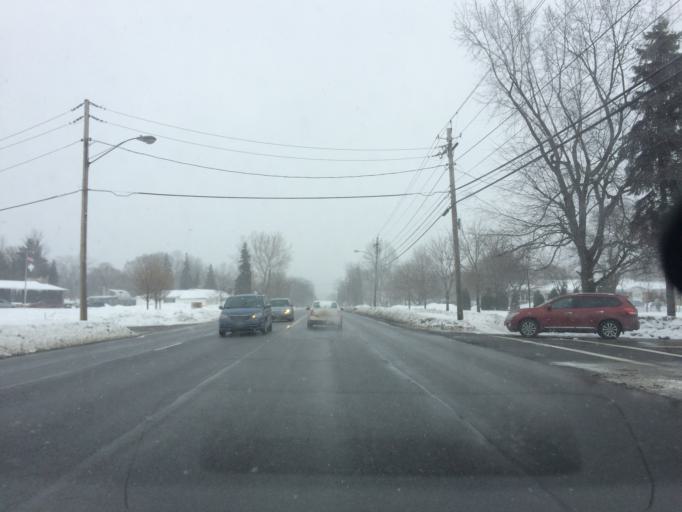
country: US
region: New York
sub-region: Monroe County
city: Rochester
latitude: 43.1257
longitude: -77.5878
